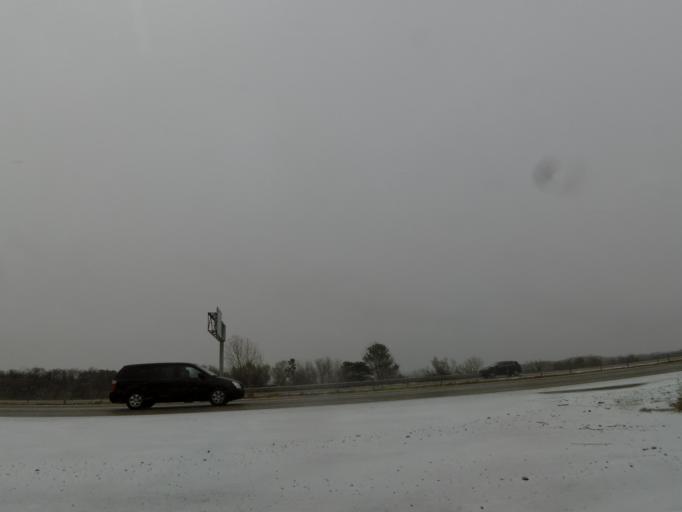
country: US
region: Minnesota
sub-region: Dakota County
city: Apple Valley
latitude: 44.7814
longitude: -93.2182
